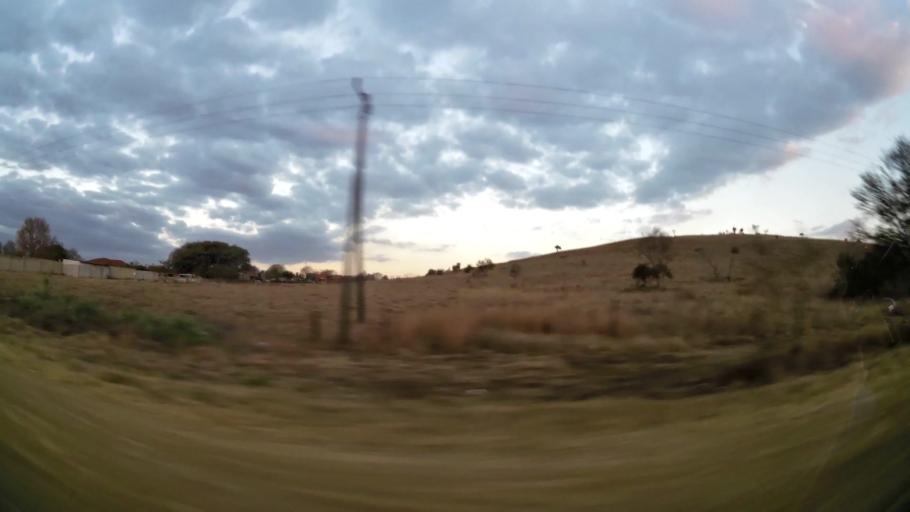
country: ZA
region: Gauteng
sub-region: West Rand District Municipality
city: Krugersdorp
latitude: -26.0362
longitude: 27.7240
